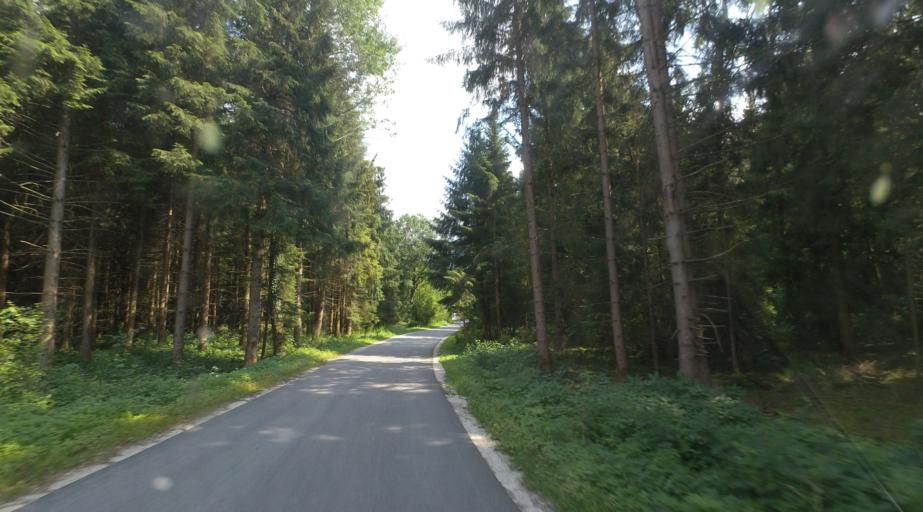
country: DE
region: Bavaria
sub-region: Upper Bavaria
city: Grabenstatt
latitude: 47.8173
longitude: 12.5512
